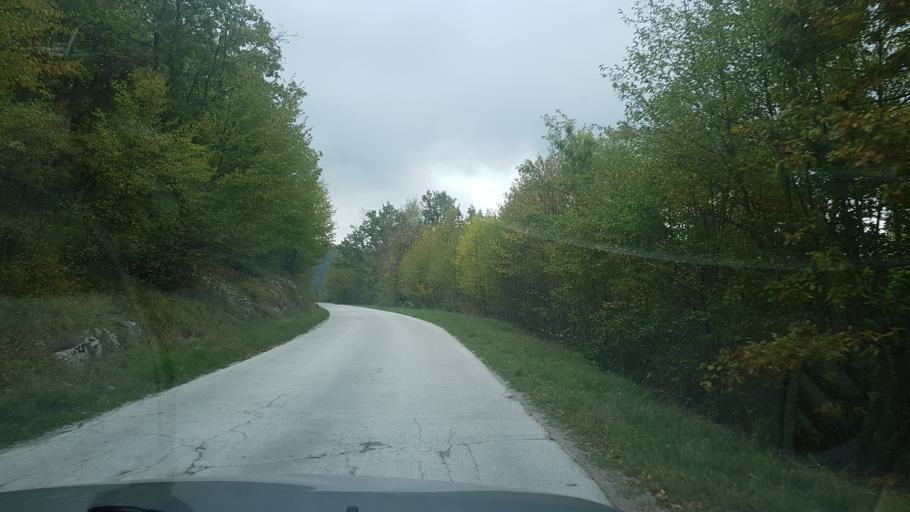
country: HR
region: Istarska
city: Buzet
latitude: 45.5046
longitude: 13.9811
